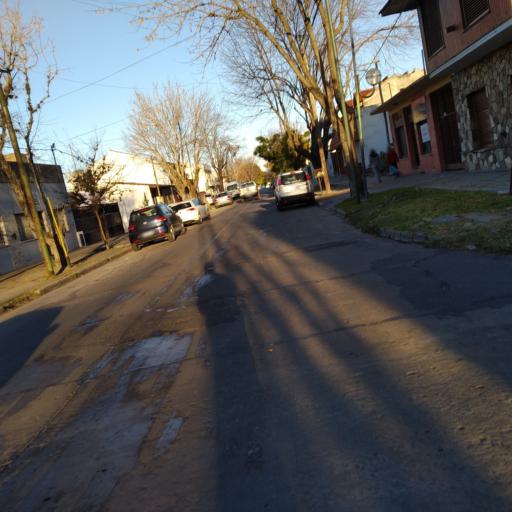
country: AR
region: Buenos Aires
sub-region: Partido de La Plata
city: La Plata
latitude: -34.9321
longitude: -57.9768
